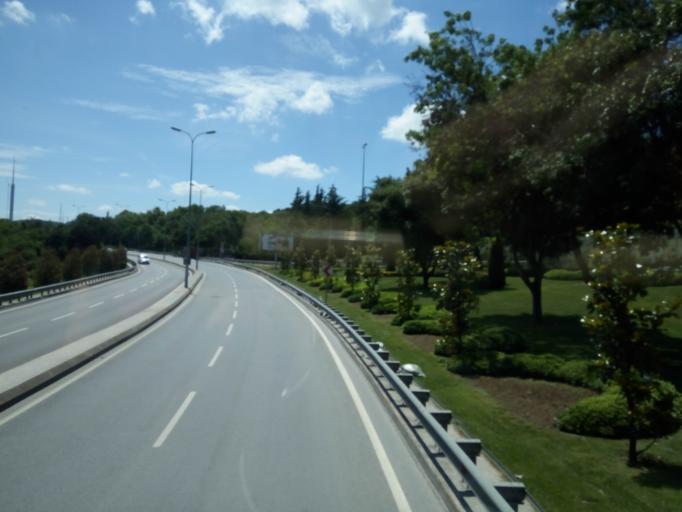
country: TR
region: Istanbul
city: UEskuedar
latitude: 41.0402
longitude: 29.0420
